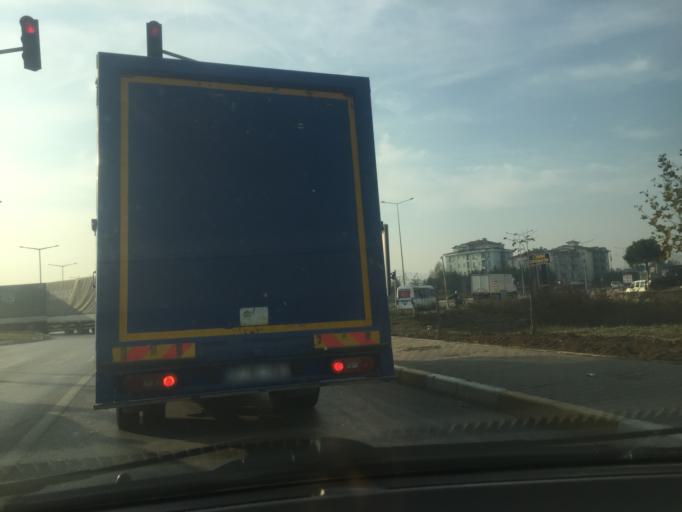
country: TR
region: Canakkale
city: Biga
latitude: 40.2341
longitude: 27.2583
